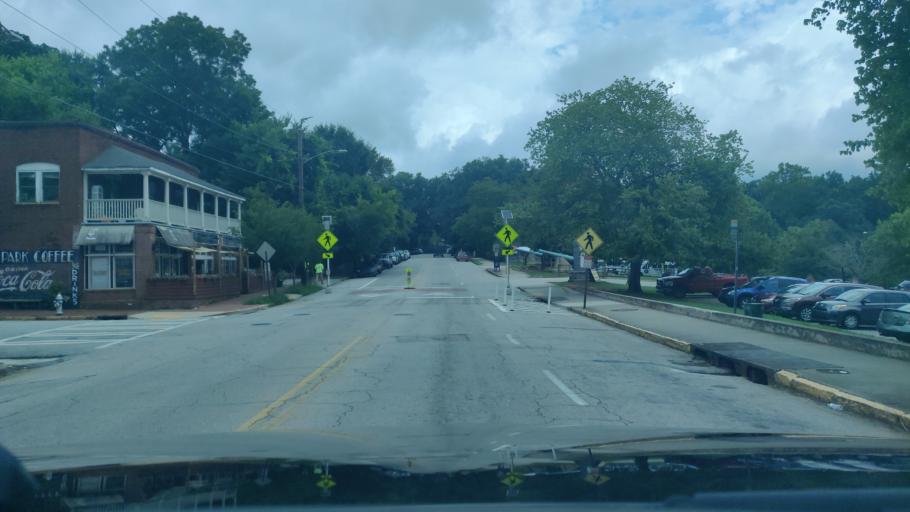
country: US
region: Georgia
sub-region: Fulton County
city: Atlanta
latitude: 33.7334
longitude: -84.3737
